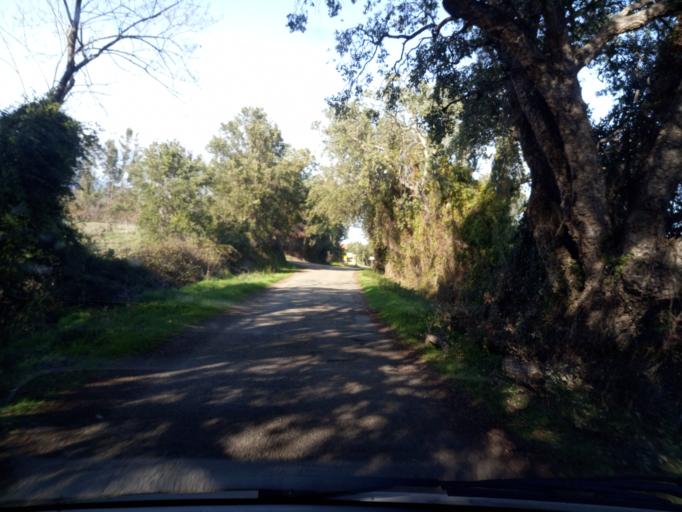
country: FR
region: Corsica
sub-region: Departement de la Haute-Corse
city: Linguizzetta
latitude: 42.2643
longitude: 9.5441
